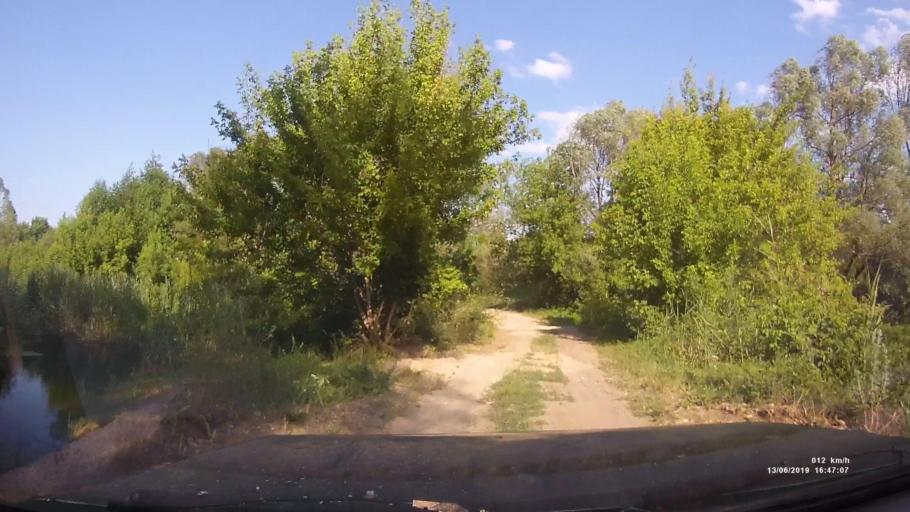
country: RU
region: Rostov
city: Kazanskaya
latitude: 49.9443
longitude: 41.4306
